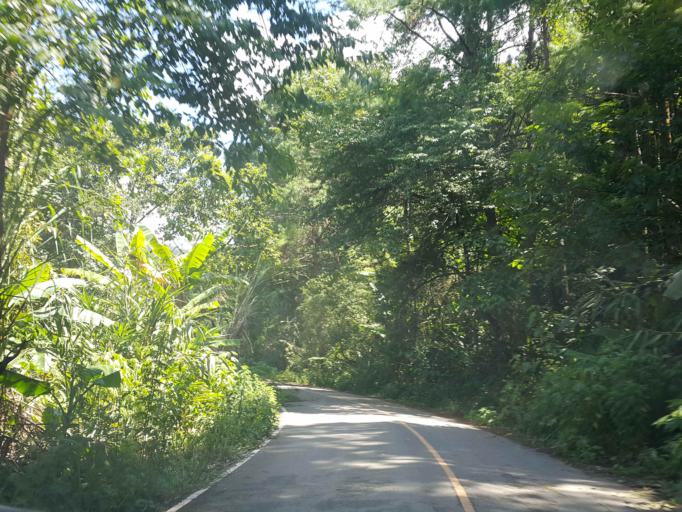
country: TH
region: Chiang Mai
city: Mae Chaem
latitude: 18.5263
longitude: 98.5221
